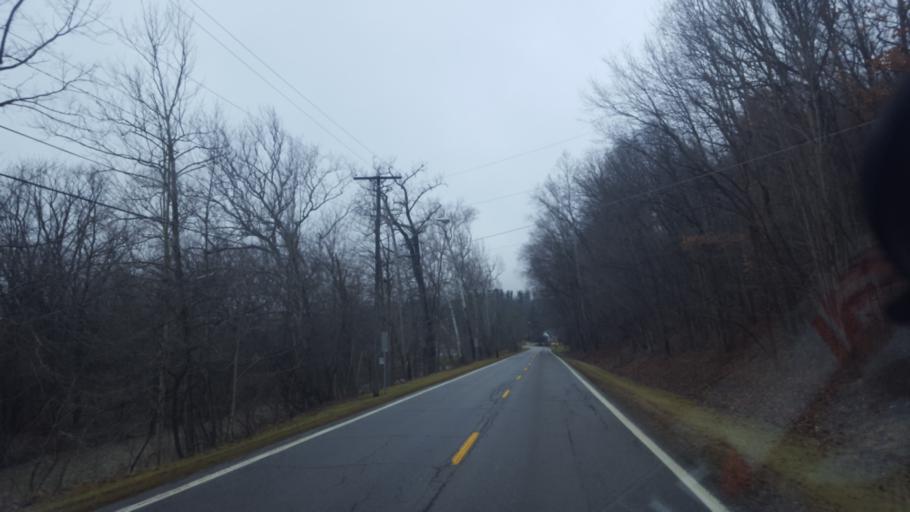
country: US
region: Ohio
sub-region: Sandusky County
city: Bellville
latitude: 40.6219
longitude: -82.5052
